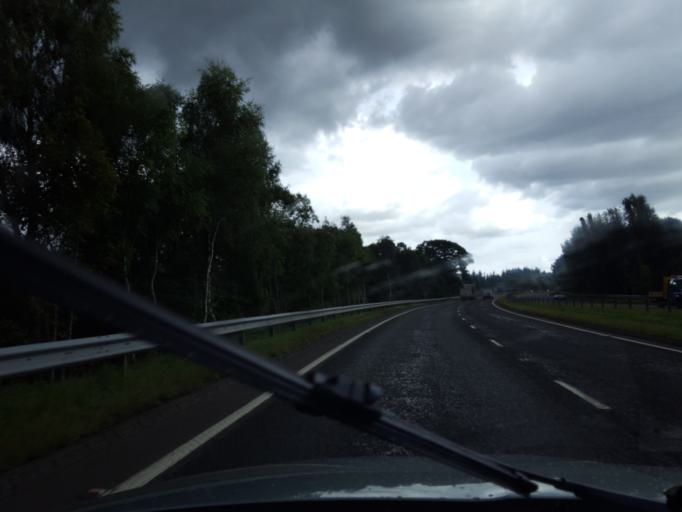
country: GB
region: Scotland
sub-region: Perth and Kinross
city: Bankfoot
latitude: 56.5349
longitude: -3.5218
